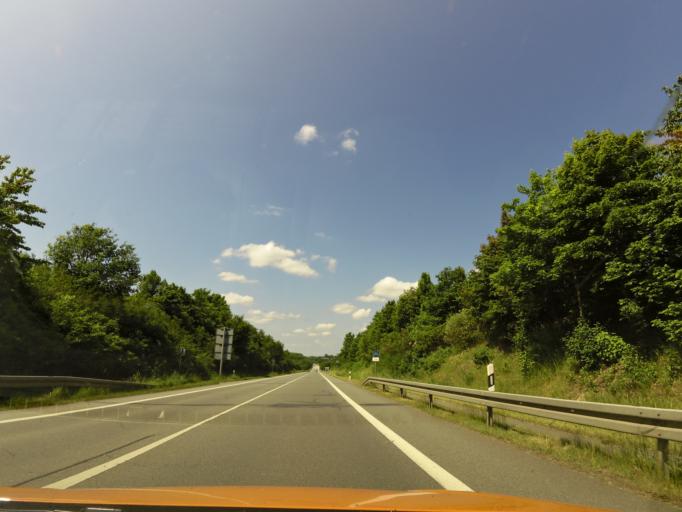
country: DE
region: Mecklenburg-Vorpommern
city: Gadebusch
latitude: 53.6897
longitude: 11.1279
